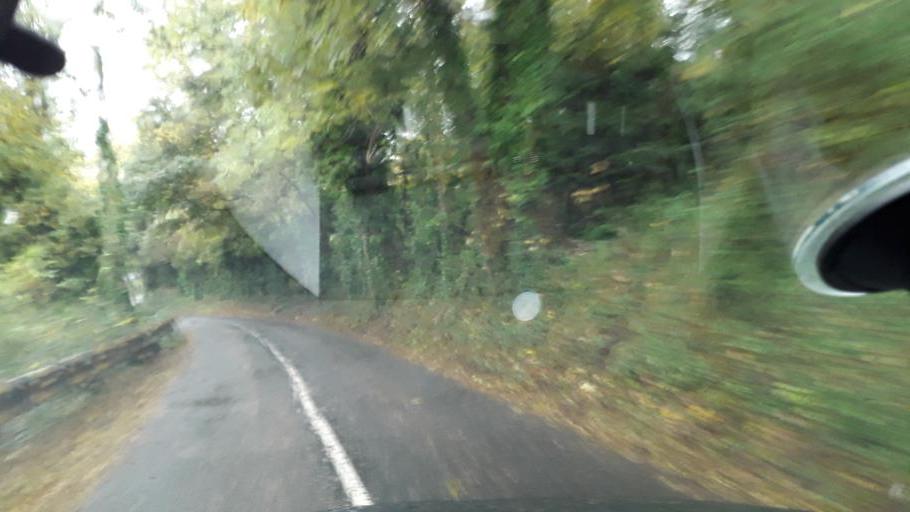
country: IE
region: Leinster
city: Ballyboden
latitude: 53.2554
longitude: -6.3015
